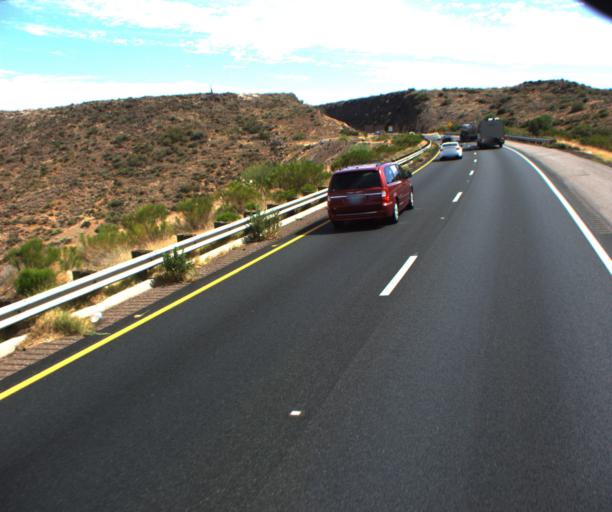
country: US
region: Arizona
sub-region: Yavapai County
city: Black Canyon City
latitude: 34.1540
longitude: -112.1398
